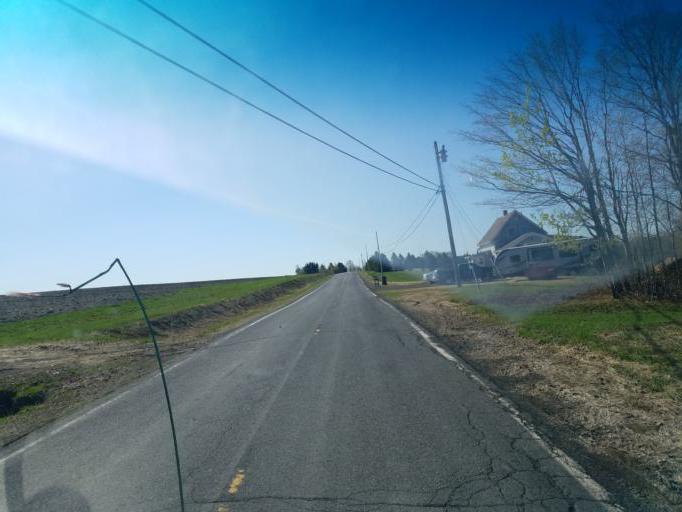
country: US
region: Maine
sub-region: Aroostook County
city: Caribou
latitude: 46.8708
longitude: -68.2123
